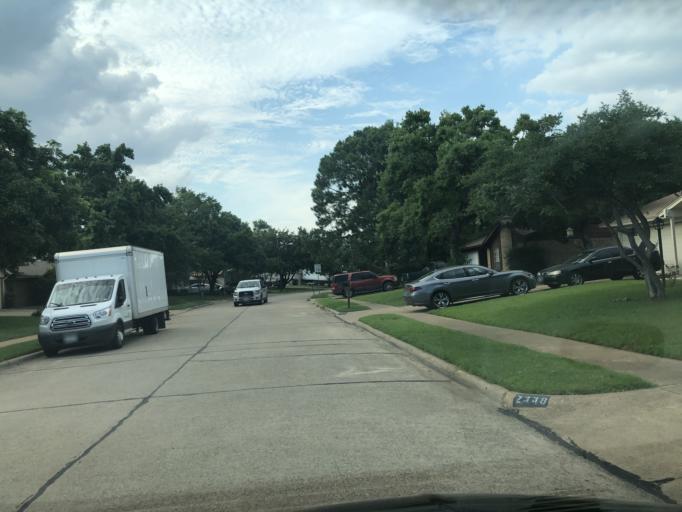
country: US
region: Texas
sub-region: Dallas County
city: Irving
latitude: 32.7925
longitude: -96.9765
